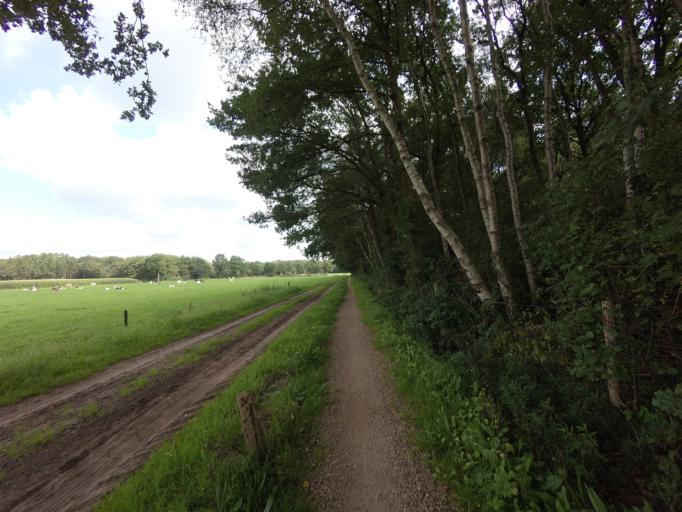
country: DE
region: Lower Saxony
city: Getelo
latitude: 52.4125
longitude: 6.8568
